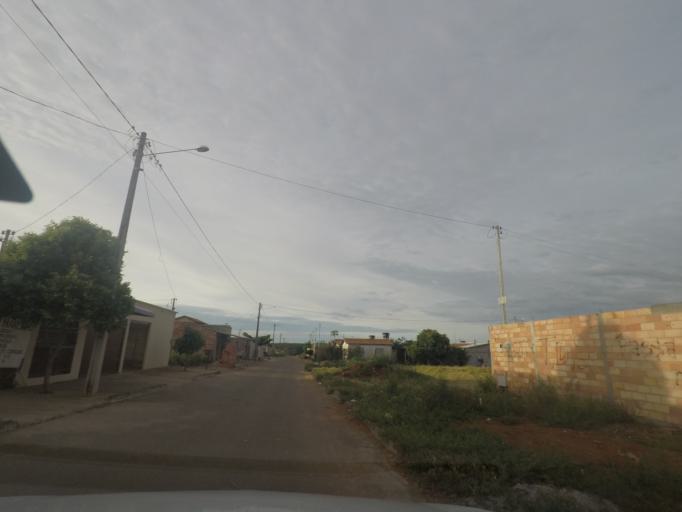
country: BR
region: Goias
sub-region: Trindade
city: Trindade
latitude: -16.7239
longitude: -49.4375
